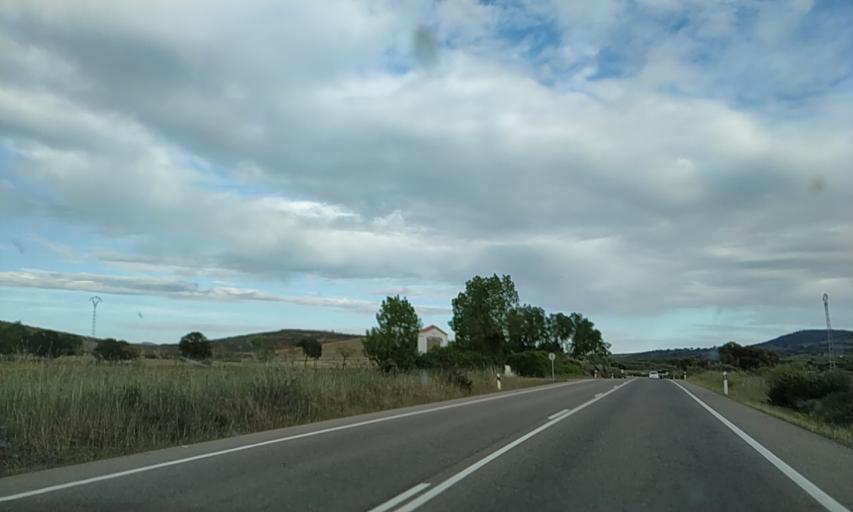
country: ES
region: Extremadura
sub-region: Provincia de Caceres
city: Pedroso de Acim
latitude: 39.8505
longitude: -6.4170
